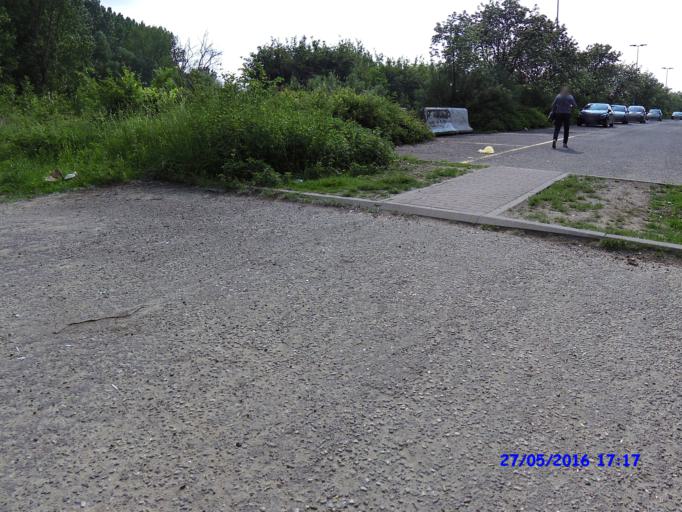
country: BE
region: Flanders
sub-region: Provincie Vlaams-Brabant
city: Wemmel
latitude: 50.8794
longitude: 4.2985
